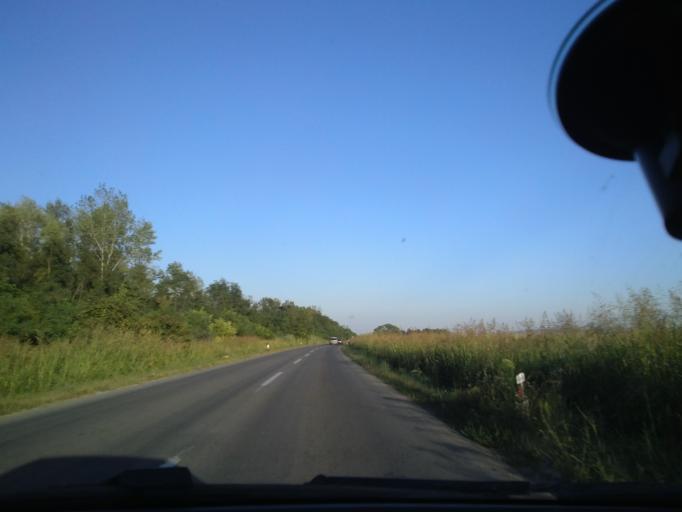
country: RS
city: Kisac
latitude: 45.3322
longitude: 19.6827
